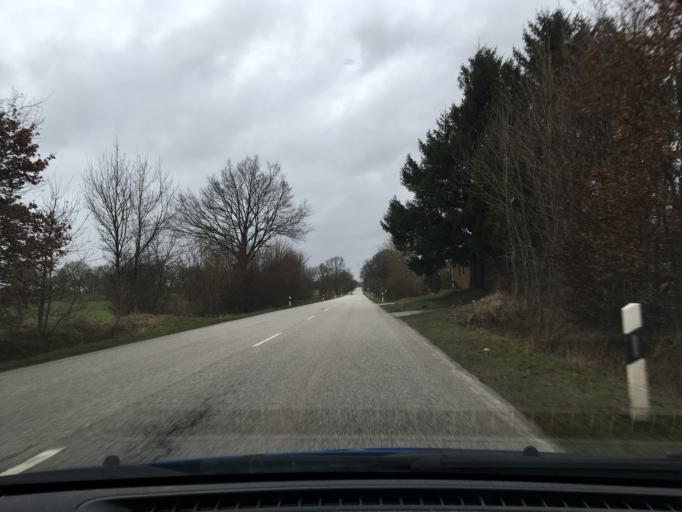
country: DE
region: Schleswig-Holstein
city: Kruzen
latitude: 53.3963
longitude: 10.5412
